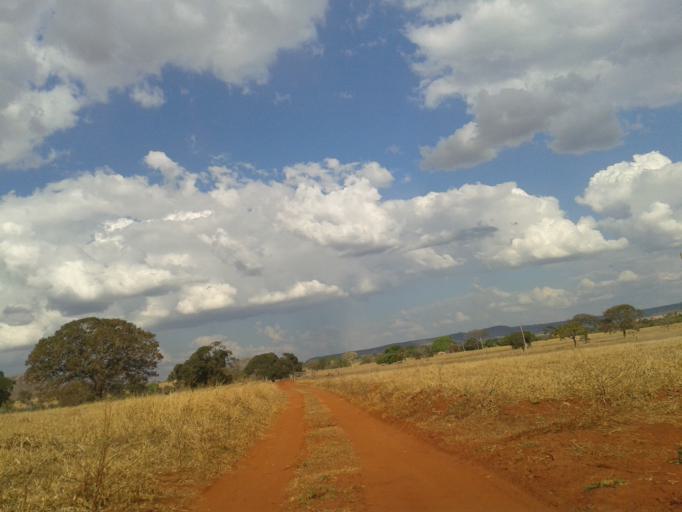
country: BR
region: Minas Gerais
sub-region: Santa Vitoria
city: Santa Vitoria
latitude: -19.1644
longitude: -50.0066
